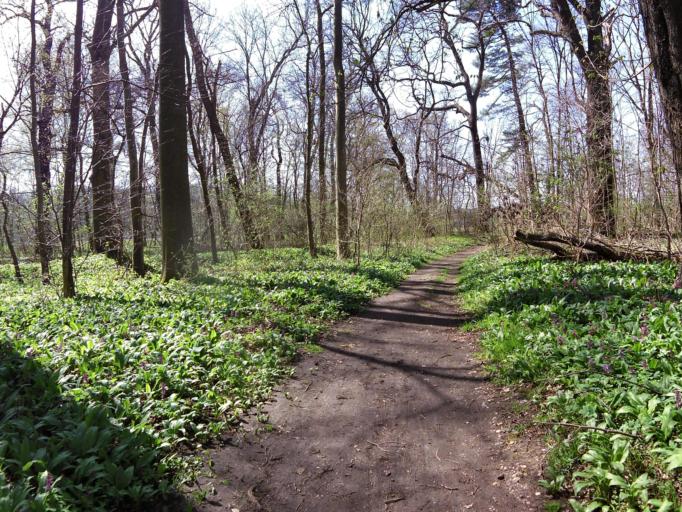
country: DE
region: Saxony
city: Schkeuditz
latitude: 51.3729
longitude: 12.2876
